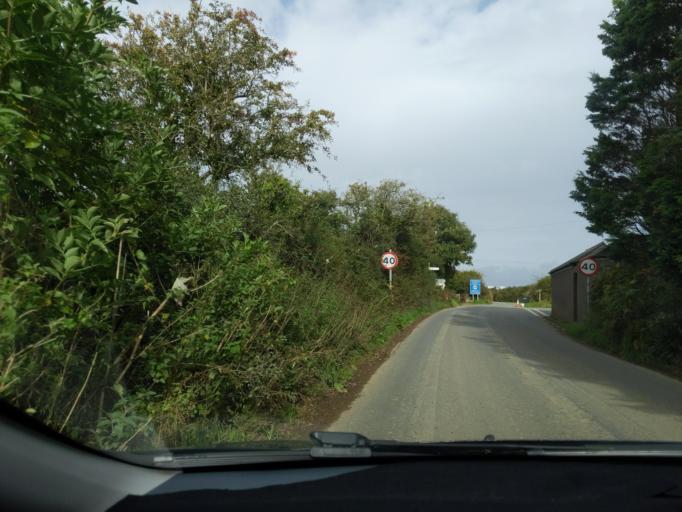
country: GB
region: England
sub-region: Cornwall
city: Mevagissey
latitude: 50.2453
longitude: -4.8044
